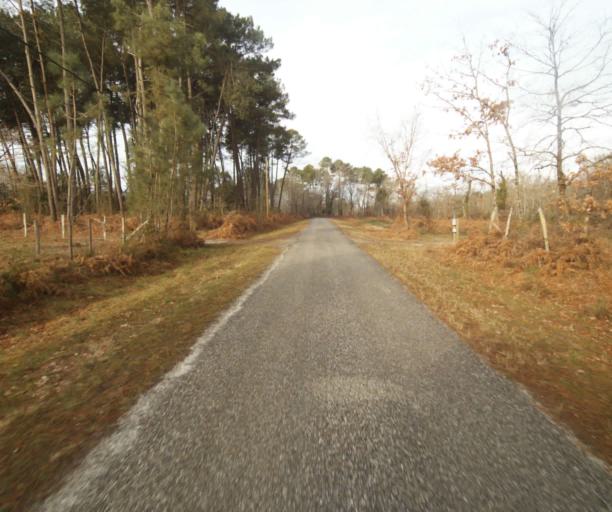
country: FR
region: Aquitaine
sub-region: Departement des Landes
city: Gabarret
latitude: 44.0730
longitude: 0.0856
